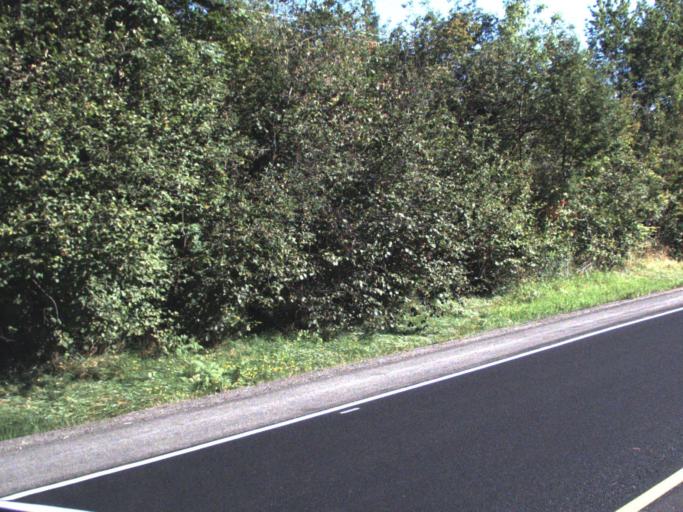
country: US
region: Washington
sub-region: King County
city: Enumclaw
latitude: 47.1848
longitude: -122.0077
